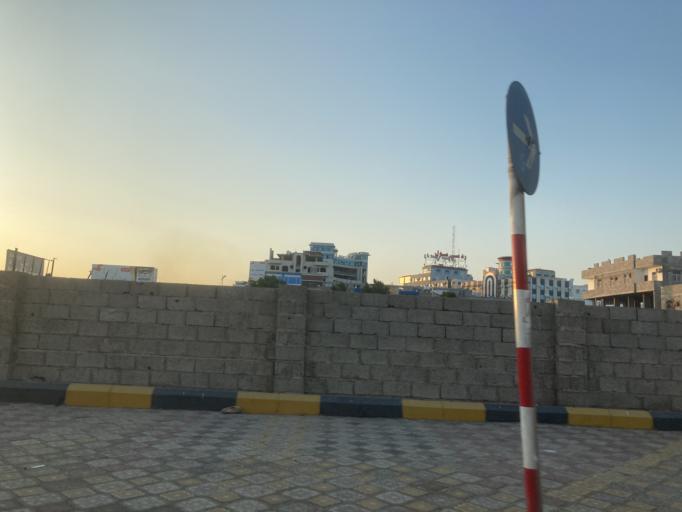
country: YE
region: Aden
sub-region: Al Mansura
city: Al Mansurah
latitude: 12.8503
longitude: 44.9906
